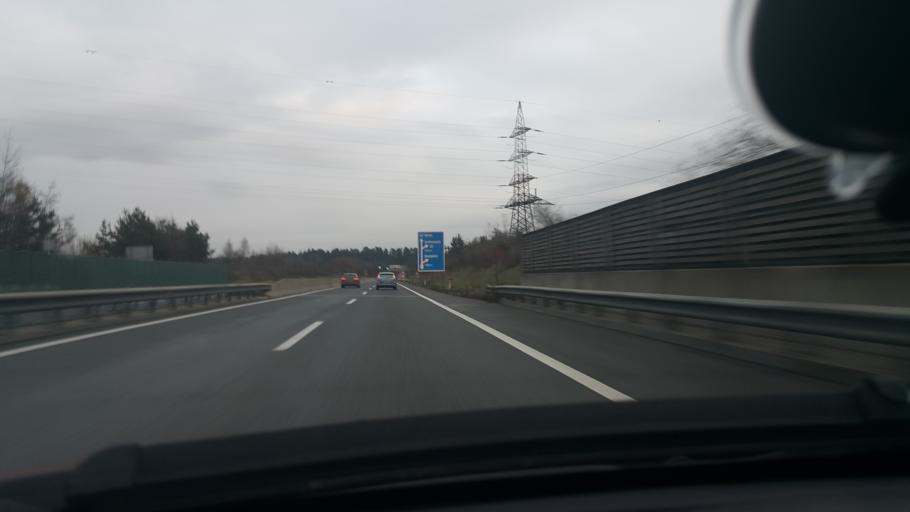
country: AT
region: Carinthia
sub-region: Politischer Bezirk Klagenfurt Land
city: Poggersdorf
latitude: 46.6445
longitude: 14.4208
